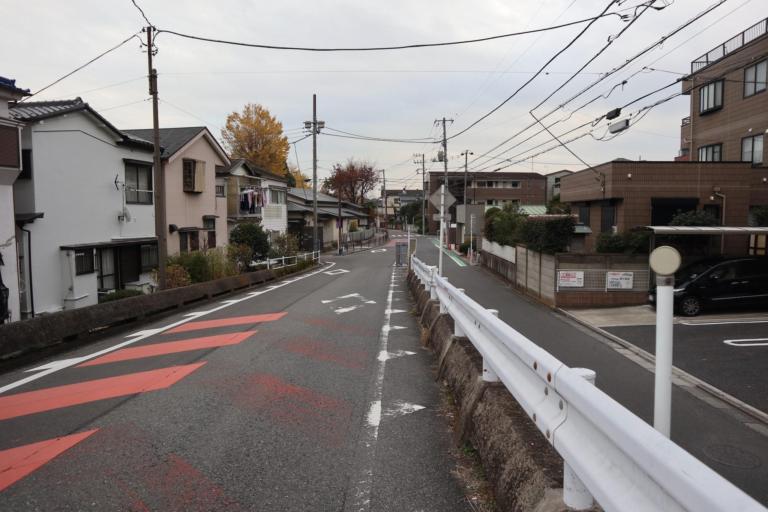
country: JP
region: Chiba
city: Matsudo
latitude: 35.7360
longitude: 139.8682
